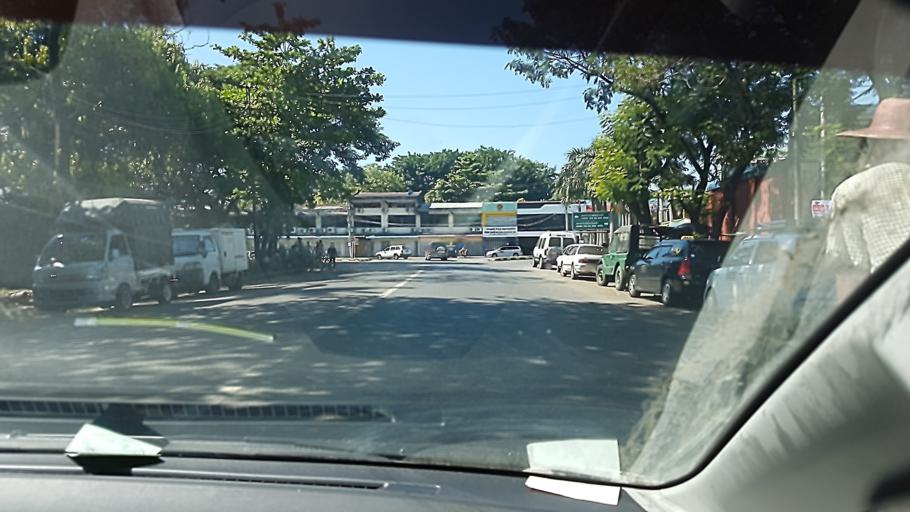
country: MM
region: Yangon
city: Yangon
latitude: 16.7836
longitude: 96.1629
